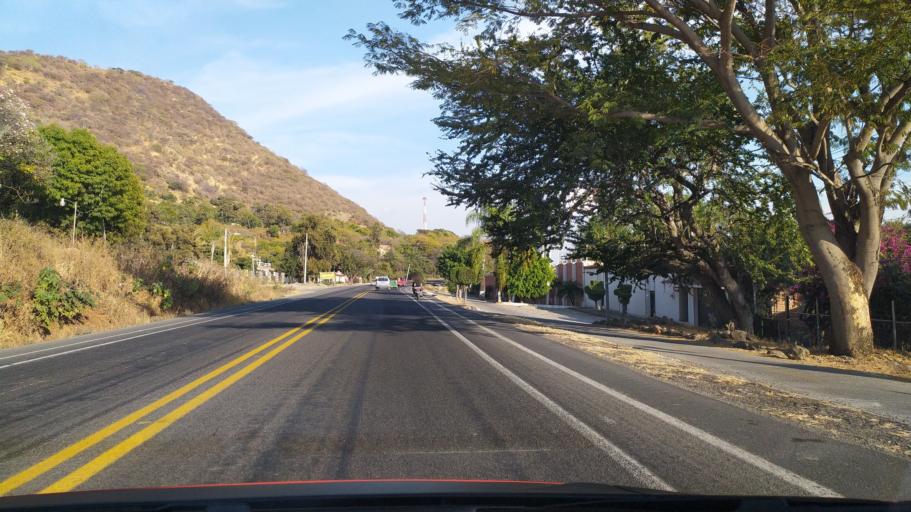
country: MX
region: Jalisco
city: Jamay
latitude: 20.2941
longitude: -102.7492
